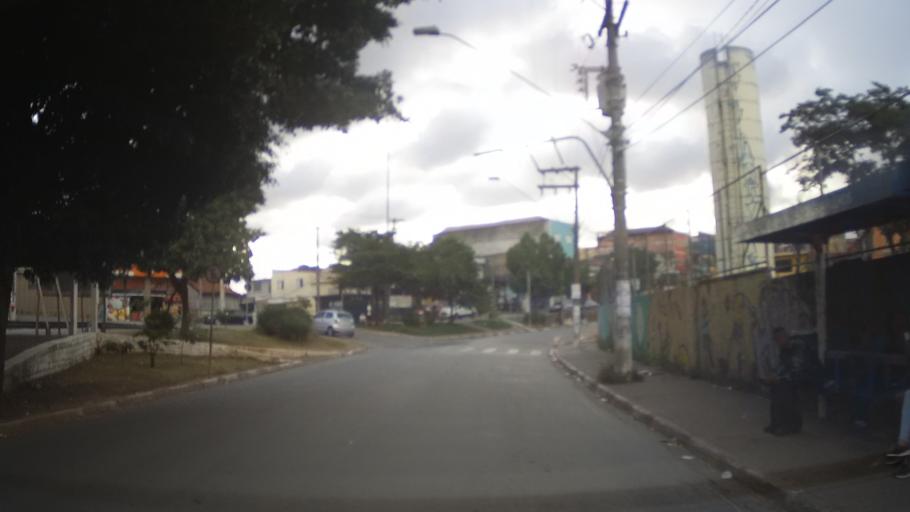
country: BR
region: Sao Paulo
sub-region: Itaquaquecetuba
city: Itaquaquecetuba
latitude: -23.4640
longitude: -46.4035
